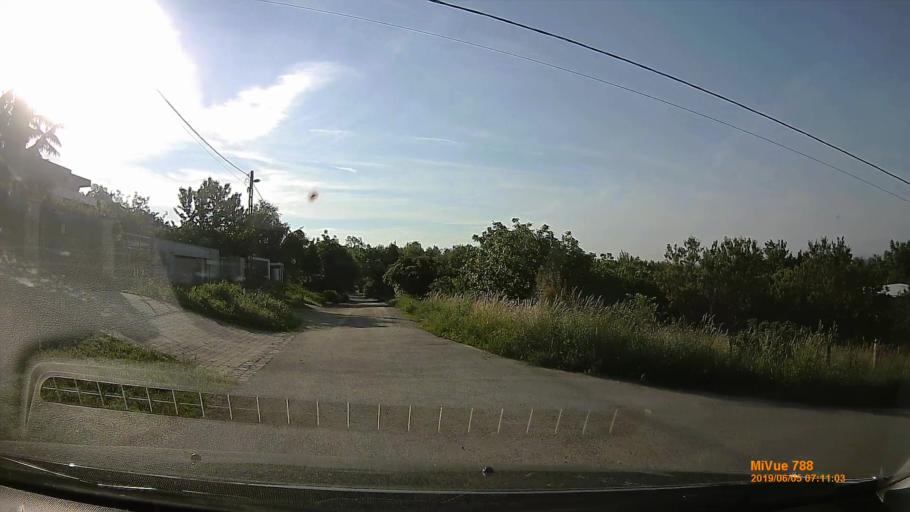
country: HU
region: Pest
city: Urom
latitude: 47.5834
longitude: 19.0303
